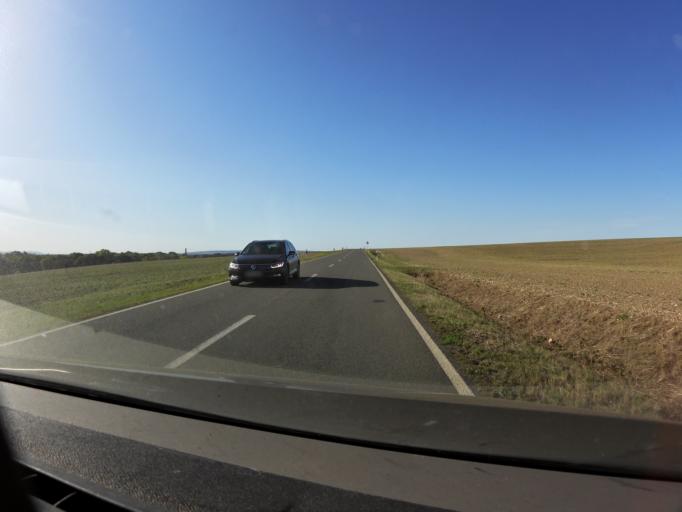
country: DE
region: Saxony-Anhalt
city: Hedersleben
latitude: 51.8721
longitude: 11.2380
